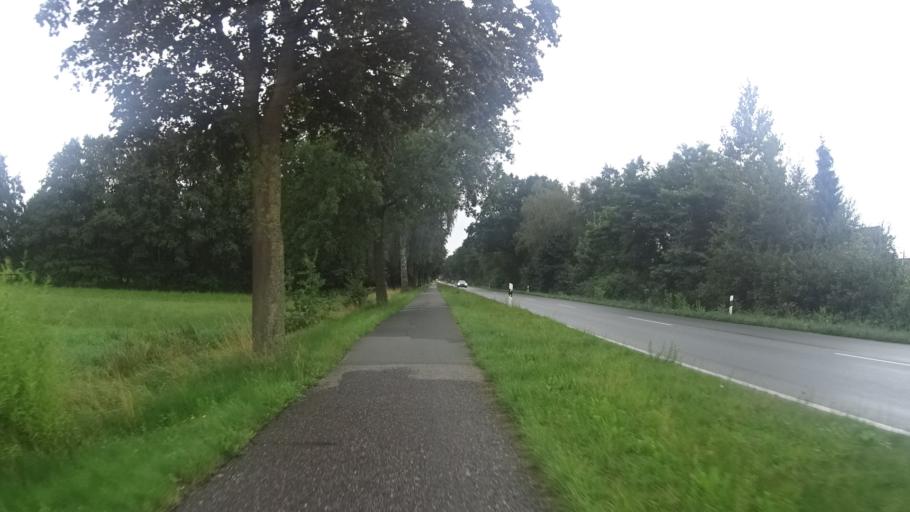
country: DE
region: Schleswig-Holstein
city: Elmshorn
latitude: 53.7720
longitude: 9.6722
